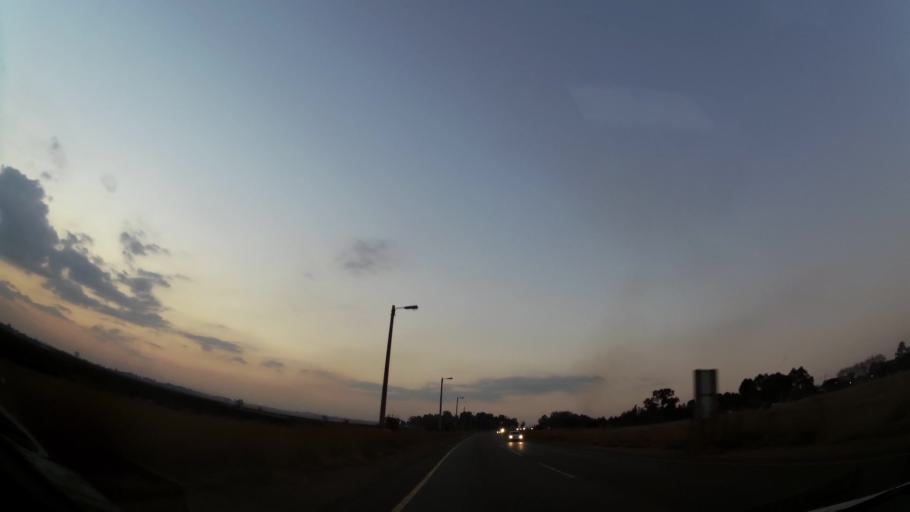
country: ZA
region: Gauteng
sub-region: Ekurhuleni Metropolitan Municipality
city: Nigel
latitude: -26.3496
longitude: 28.4542
